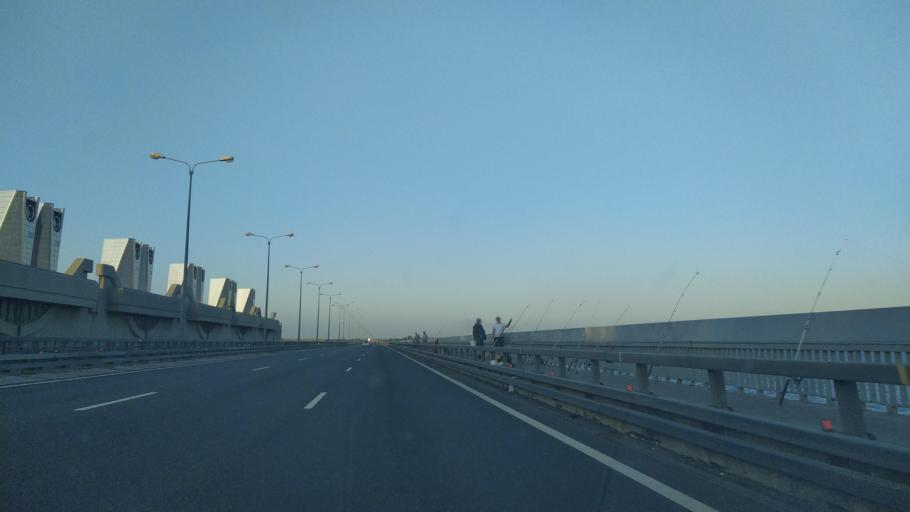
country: RU
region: Leningrad
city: Gorskaya
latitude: 60.0323
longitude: 29.9041
